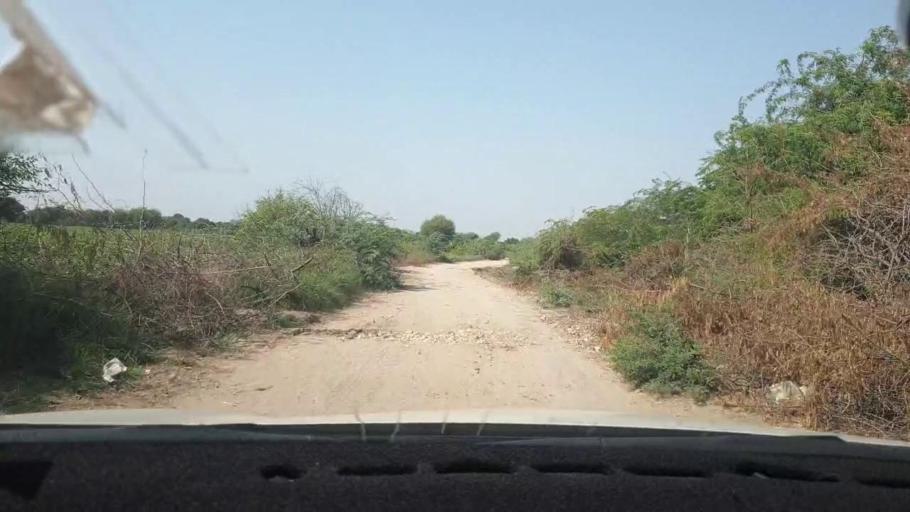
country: PK
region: Sindh
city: Tando Mittha Khan
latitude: 25.8633
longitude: 69.3849
